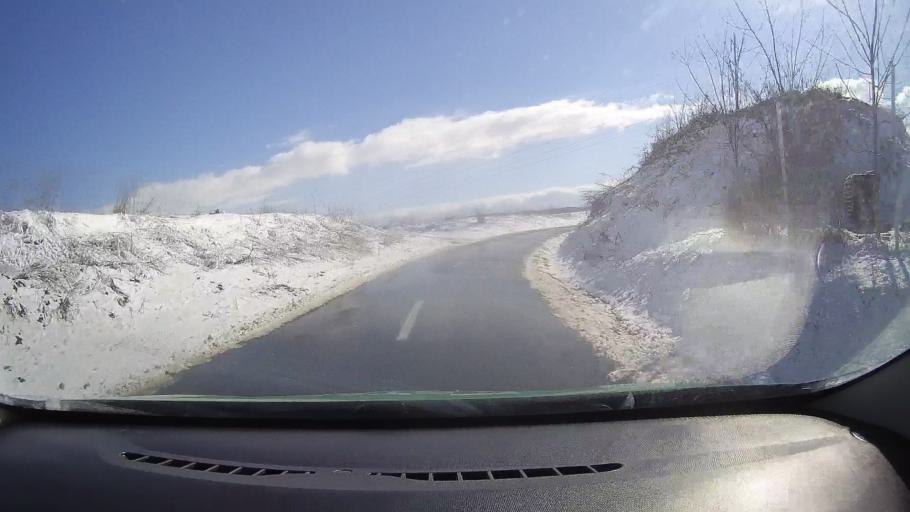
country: RO
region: Sibiu
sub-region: Comuna Rosia
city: Rosia
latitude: 45.7969
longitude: 24.2928
